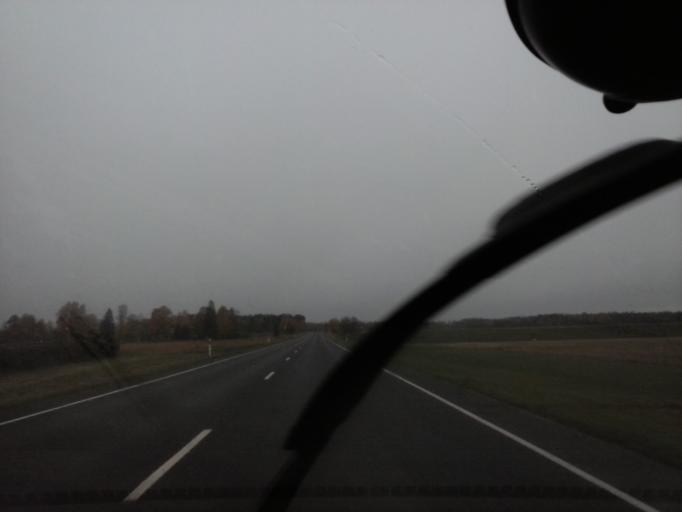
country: EE
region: Viljandimaa
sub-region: Vohma linn
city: Vohma
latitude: 58.7024
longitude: 25.6230
